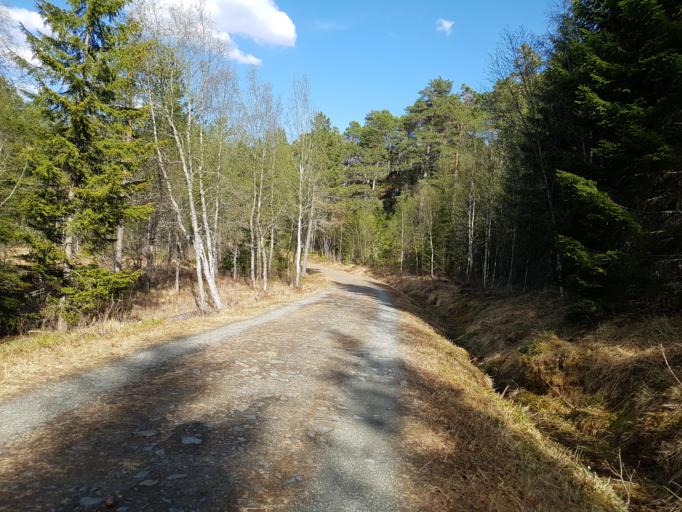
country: NO
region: Sor-Trondelag
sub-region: Trondheim
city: Trondheim
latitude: 63.4409
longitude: 10.3130
